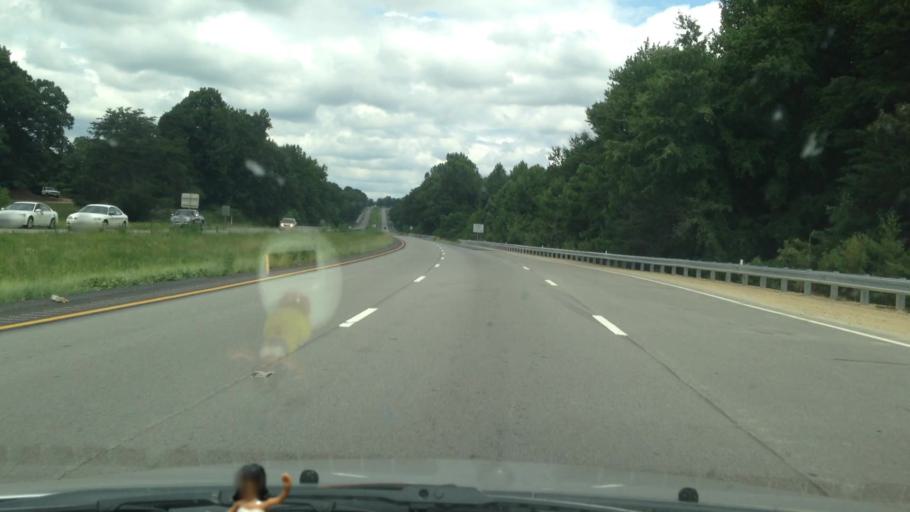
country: US
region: Virginia
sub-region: Pittsylvania County
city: Chatham
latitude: 36.8353
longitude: -79.3816
